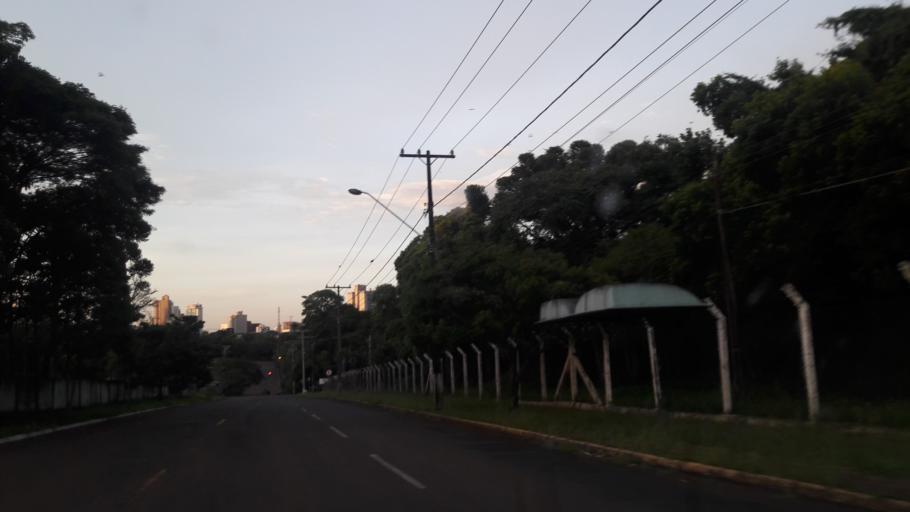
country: BR
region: Parana
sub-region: Cascavel
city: Cascavel
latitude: -24.9609
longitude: -53.4500
